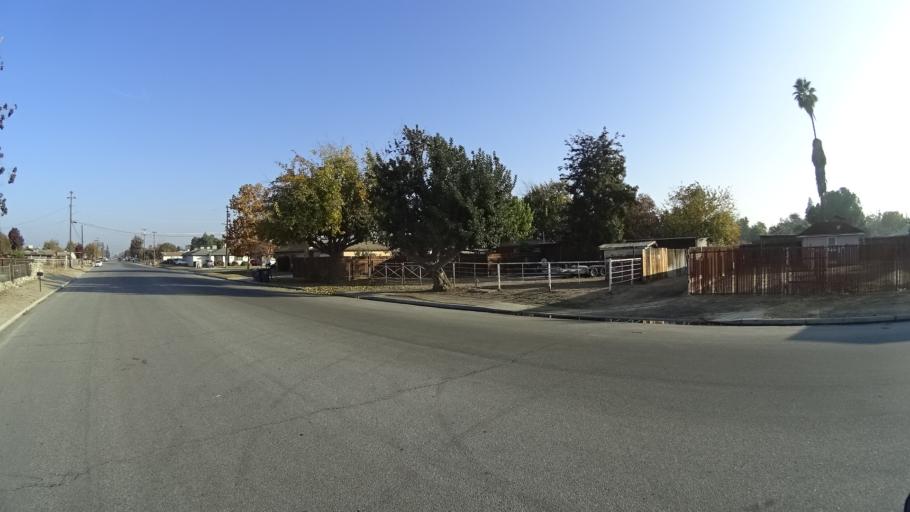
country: US
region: California
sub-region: Kern County
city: Greenacres
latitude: 35.3790
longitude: -119.1190
